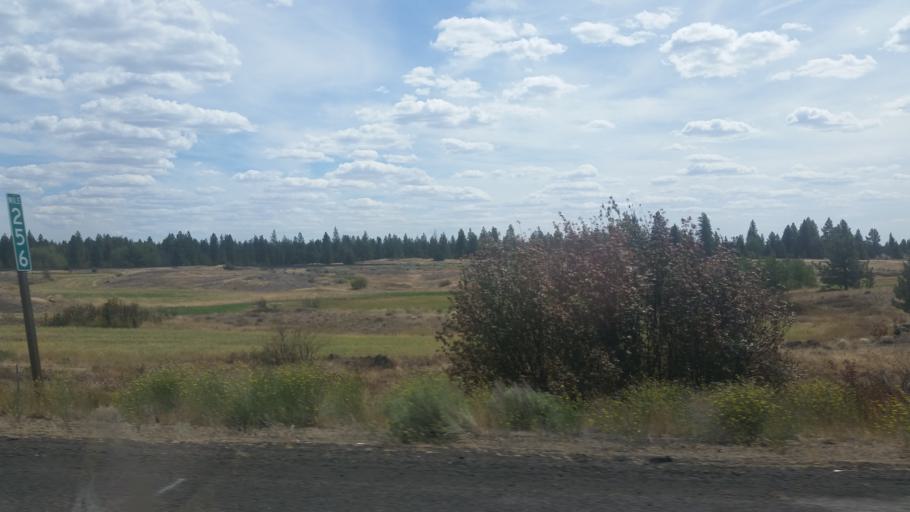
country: US
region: Washington
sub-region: Spokane County
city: Medical Lake
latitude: 47.4173
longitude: -117.8134
